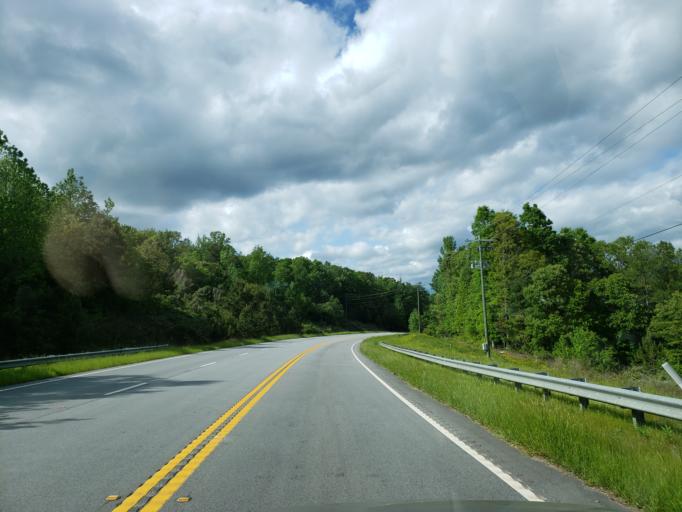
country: US
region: Georgia
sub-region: Carroll County
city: Mount Zion
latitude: 33.6392
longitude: -85.2775
